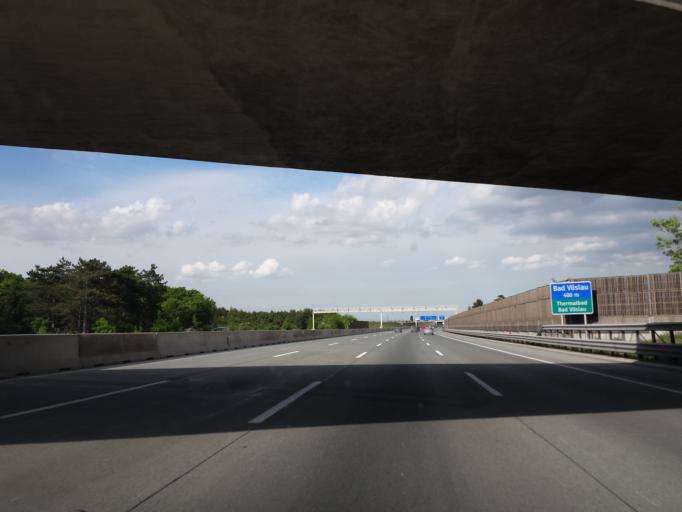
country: AT
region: Lower Austria
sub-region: Politischer Bezirk Baden
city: Kottingbrunn
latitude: 47.9668
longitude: 16.2328
